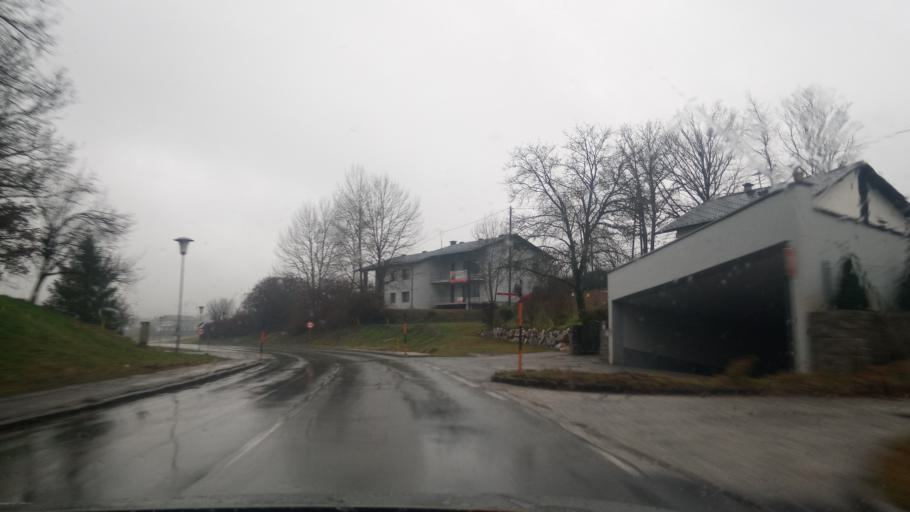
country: AT
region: Carinthia
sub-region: Politischer Bezirk Klagenfurt Land
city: Kottmannsdorf
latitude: 46.5883
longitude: 14.2344
